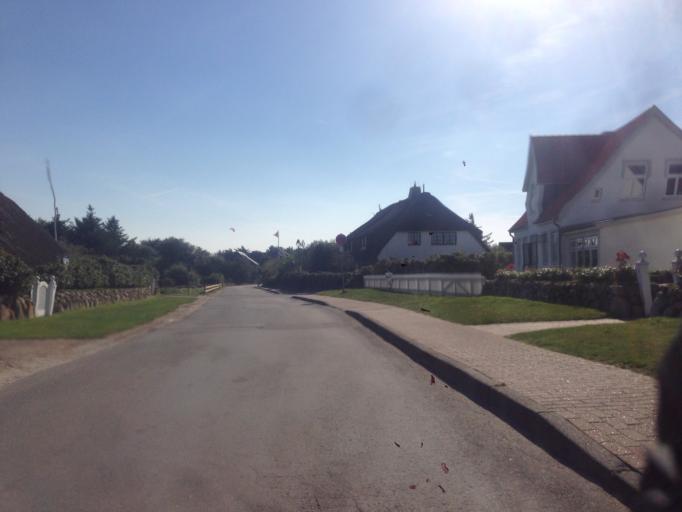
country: DE
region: Schleswig-Holstein
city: Westerland
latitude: 54.9394
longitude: 8.3255
